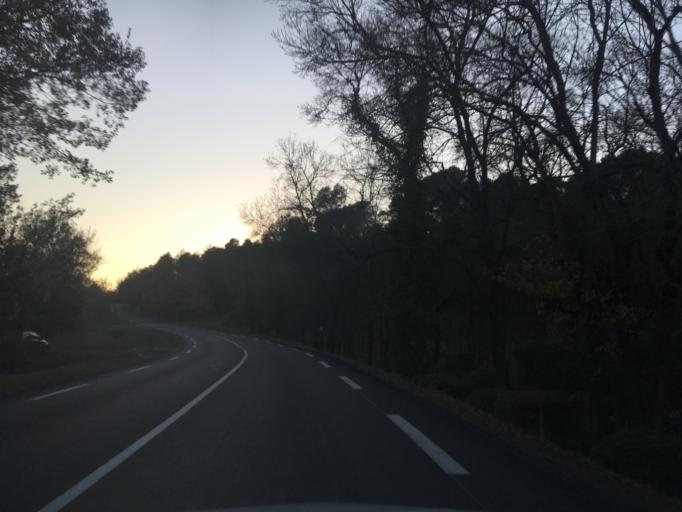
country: FR
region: Provence-Alpes-Cote d'Azur
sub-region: Departement des Alpes-Maritimes
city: Le Tignet
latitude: 43.6118
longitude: 6.8160
